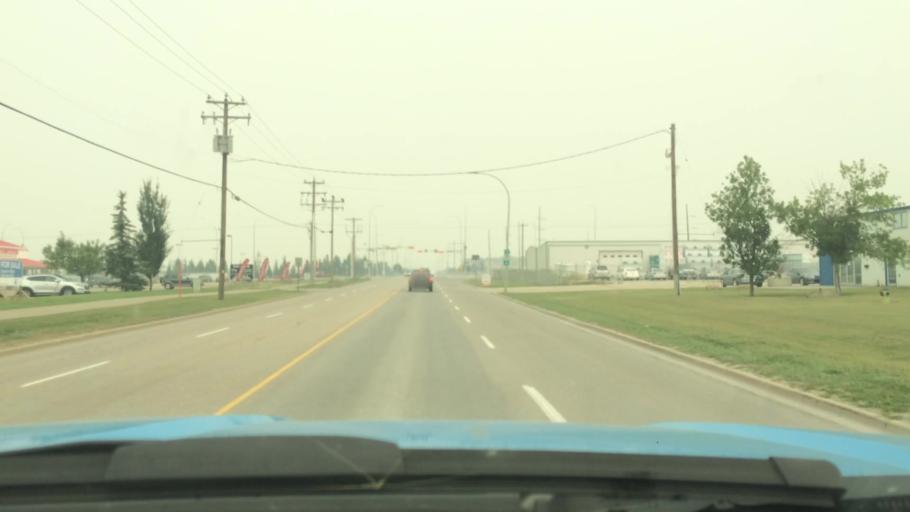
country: CA
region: Alberta
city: Airdrie
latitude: 51.2982
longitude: -113.9900
